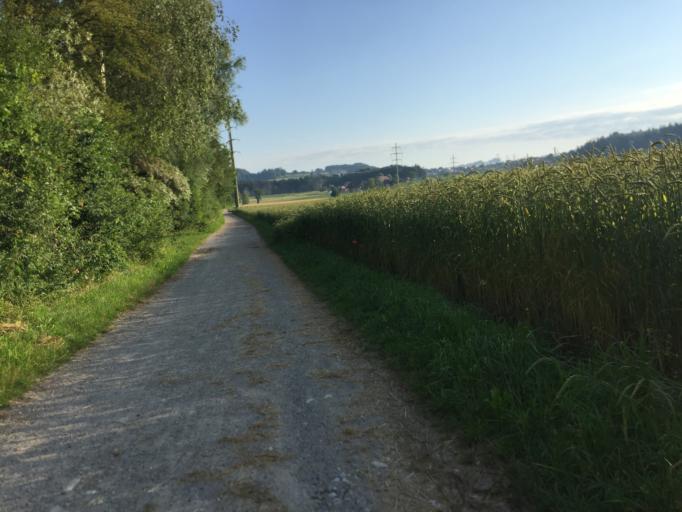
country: CH
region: Bern
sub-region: Bern-Mittelland District
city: Rubigen
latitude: 46.9129
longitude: 7.5382
